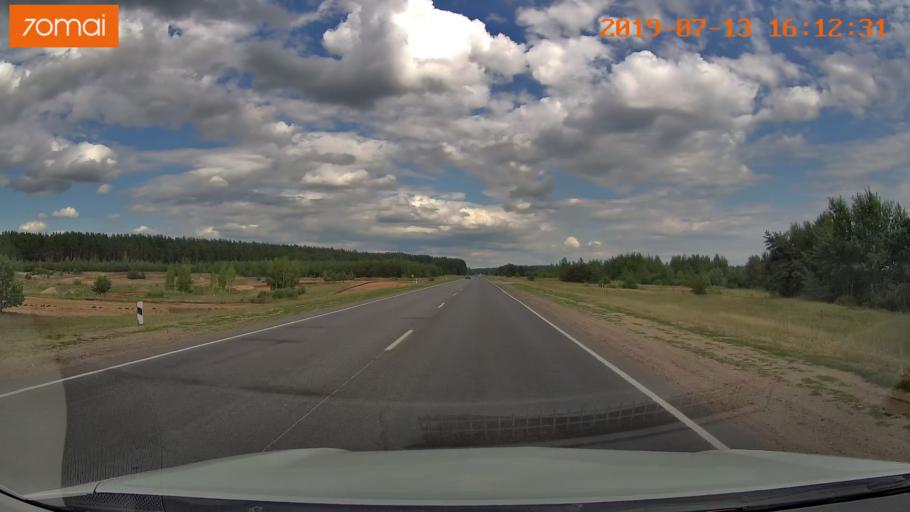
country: BY
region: Mogilev
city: Babruysk
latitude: 53.1667
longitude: 29.2820
